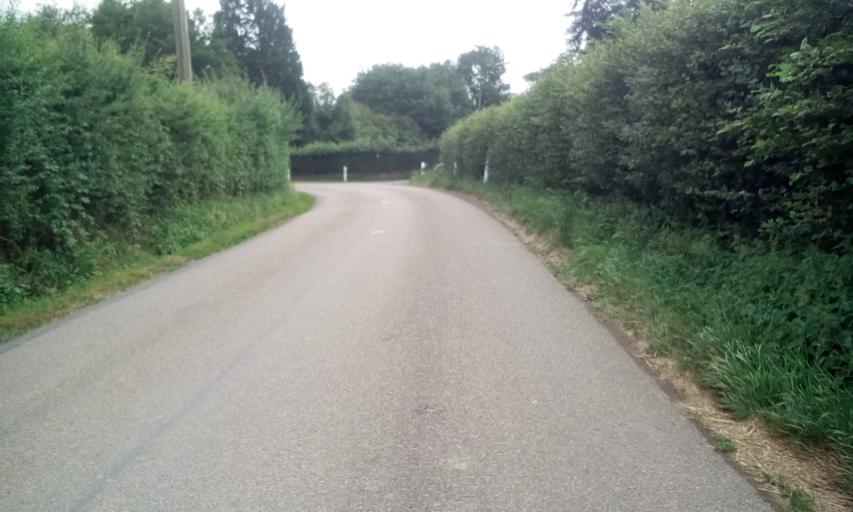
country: FR
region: Lower Normandy
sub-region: Departement du Calvados
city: Bavent
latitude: 49.2135
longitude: -0.1797
